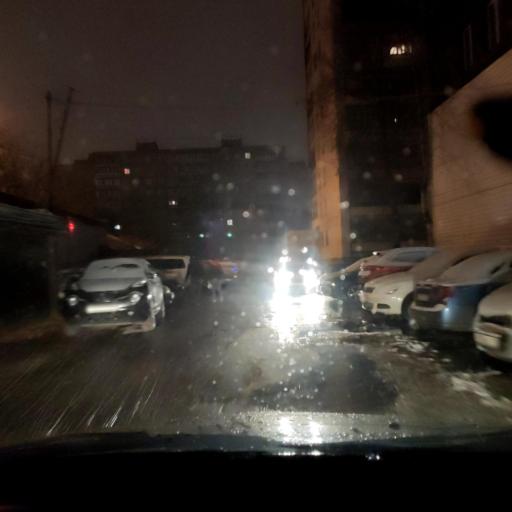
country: RU
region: Bashkortostan
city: Ufa
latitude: 54.7335
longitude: 55.9938
